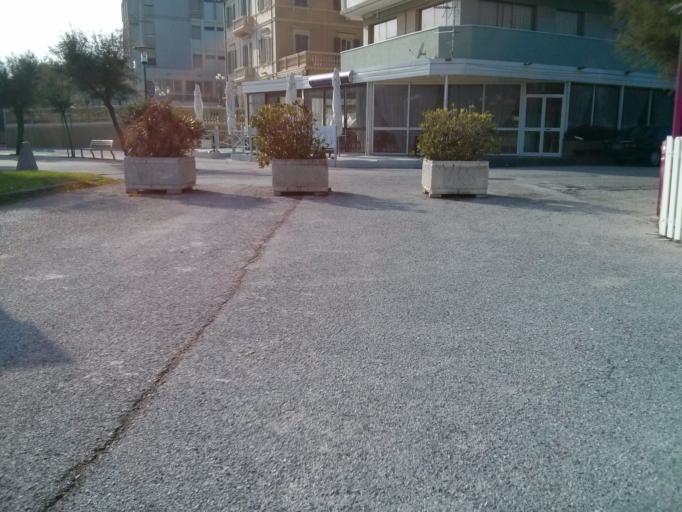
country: IT
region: The Marches
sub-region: Provincia di Pesaro e Urbino
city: Pesaro
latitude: 43.9147
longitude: 12.9184
